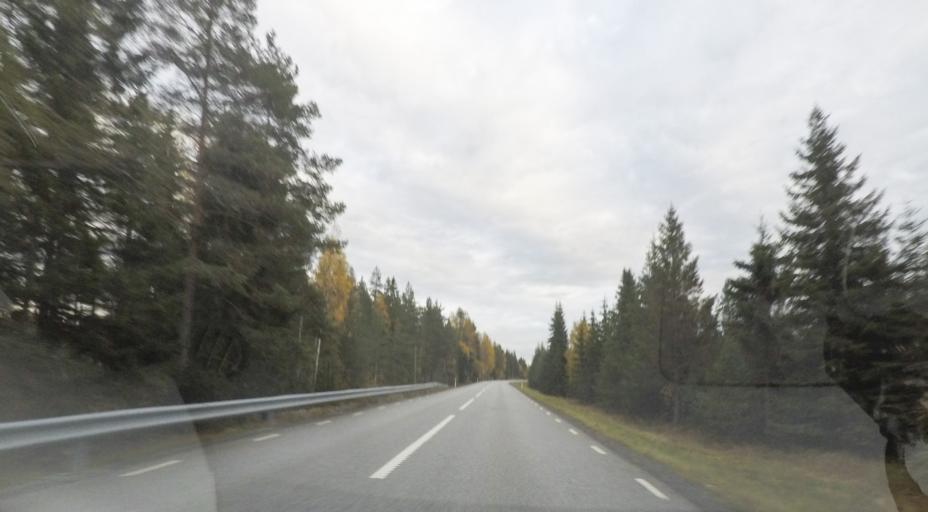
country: SE
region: OErebro
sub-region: Nora Kommun
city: As
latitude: 59.5309
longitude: 14.8176
